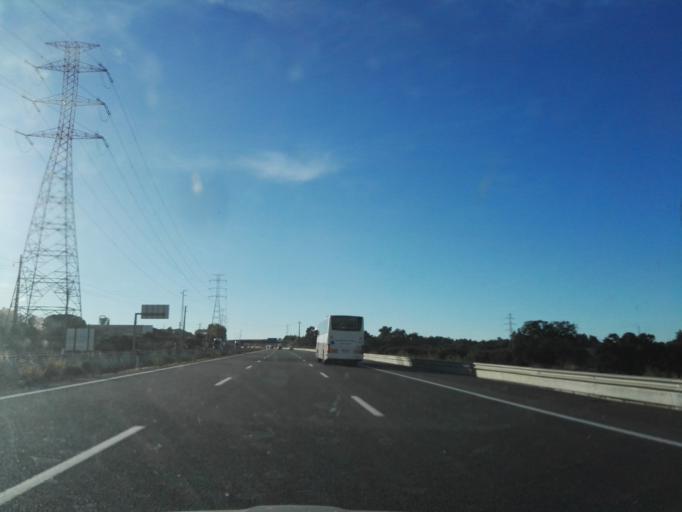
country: PT
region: Setubal
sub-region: Palmela
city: Palmela
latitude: 38.5830
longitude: -8.8773
